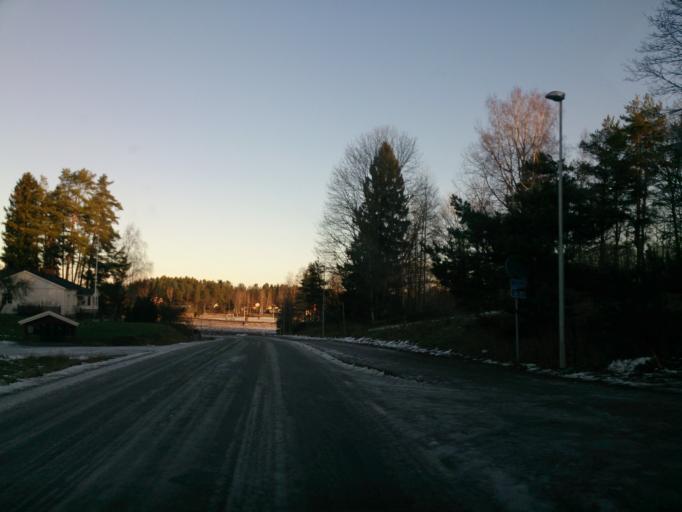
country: SE
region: OEstergoetland
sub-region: Linkopings Kommun
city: Sturefors
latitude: 58.3078
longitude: 15.8725
